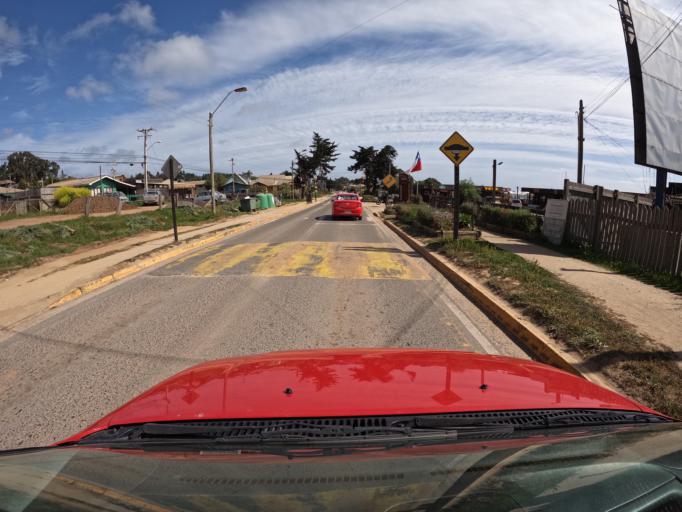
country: CL
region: O'Higgins
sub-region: Provincia de Colchagua
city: Santa Cruz
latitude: -34.4088
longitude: -72.0265
